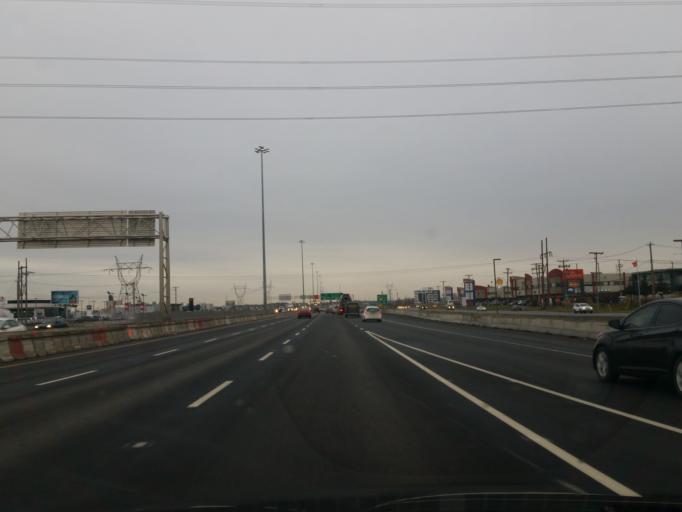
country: CA
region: Quebec
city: Quebec
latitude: 46.8354
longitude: -71.2687
